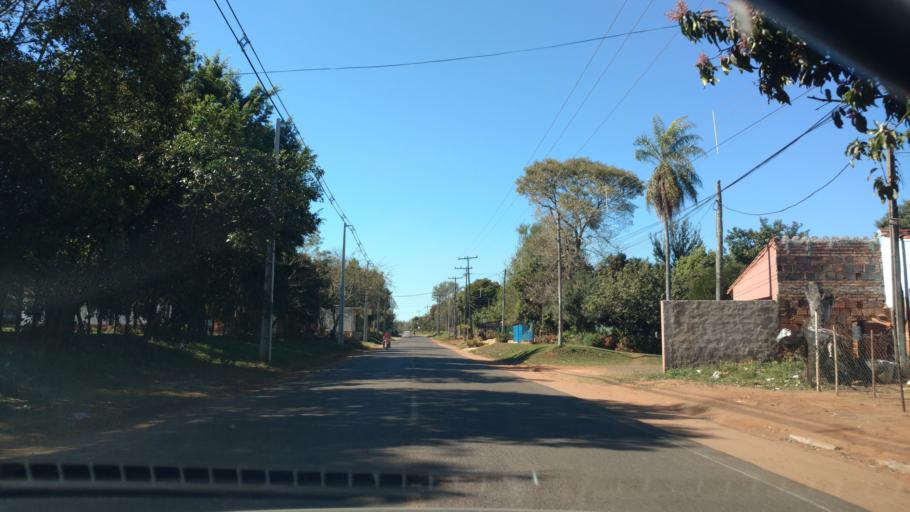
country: PY
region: Central
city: Itaugua
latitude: -25.4033
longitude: -57.3358
